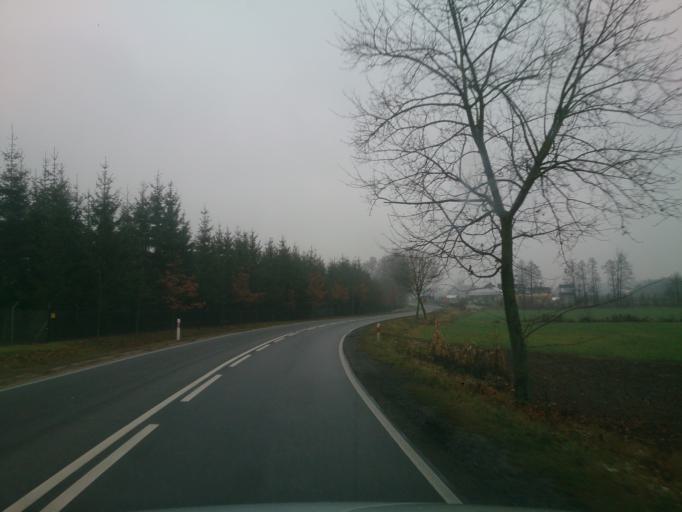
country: PL
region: Kujawsko-Pomorskie
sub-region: Powiat rypinski
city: Rypin
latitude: 53.1203
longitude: 19.3855
